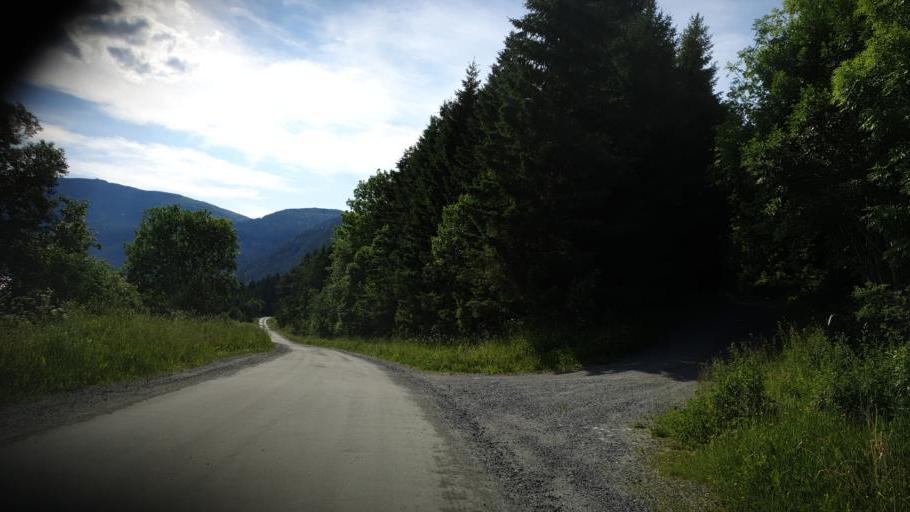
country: NO
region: Sor-Trondelag
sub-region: Trondheim
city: Trondheim
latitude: 63.5754
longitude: 10.3906
